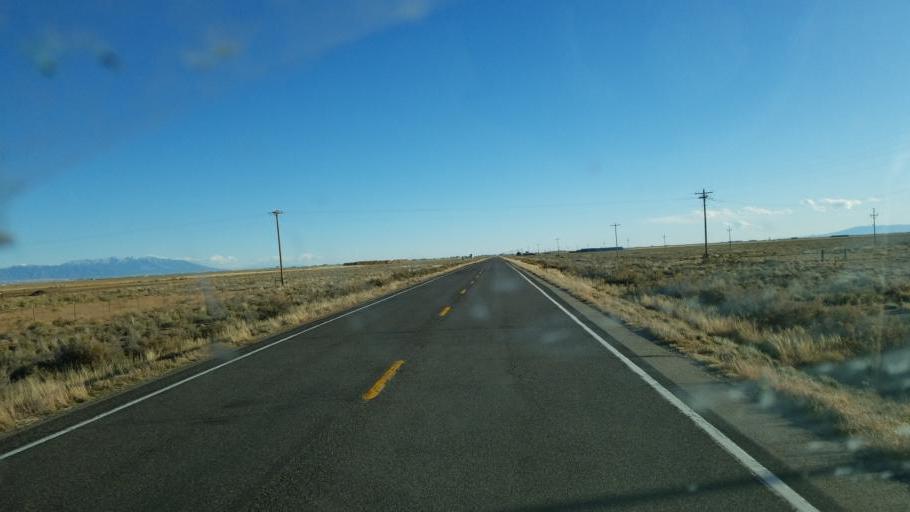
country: US
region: Colorado
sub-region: Saguache County
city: Saguache
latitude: 38.1235
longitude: -105.9222
